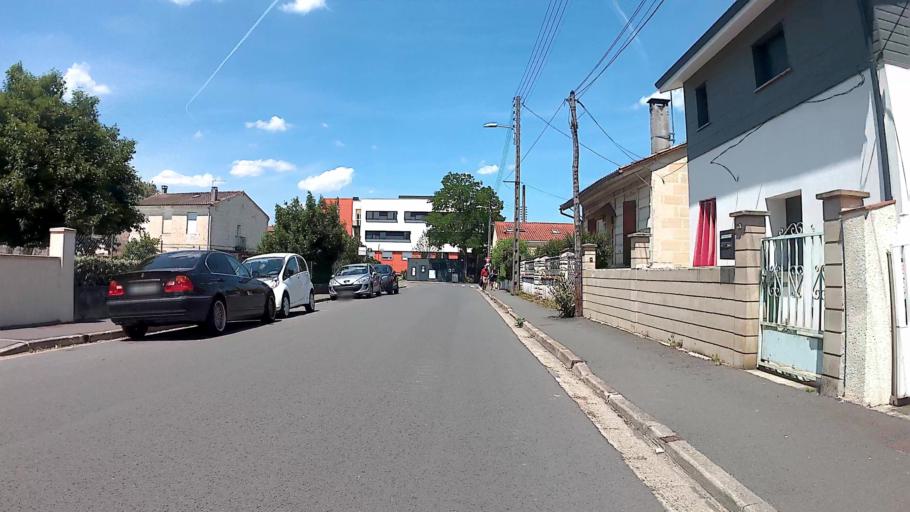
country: FR
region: Aquitaine
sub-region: Departement de la Gironde
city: Talence
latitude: 44.8054
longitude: -0.5742
